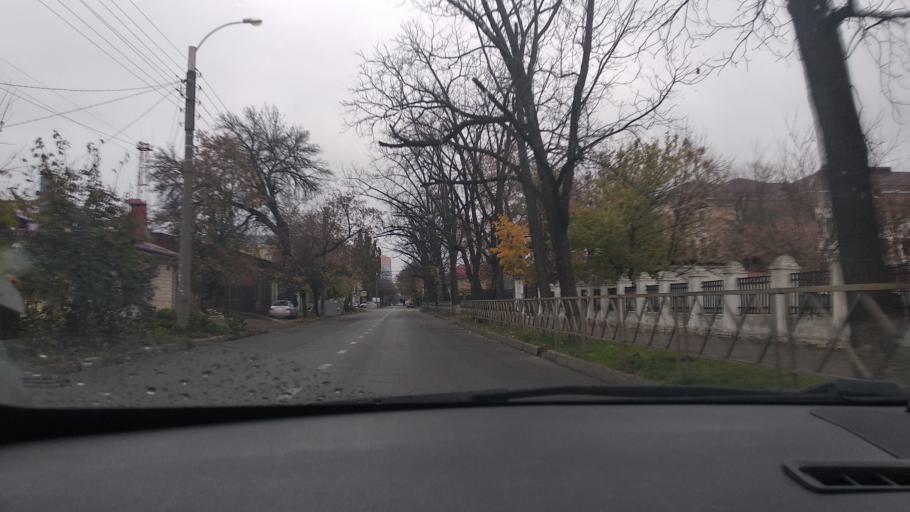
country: RU
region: Krasnodarskiy
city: Krasnodar
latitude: 45.0300
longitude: 38.9835
